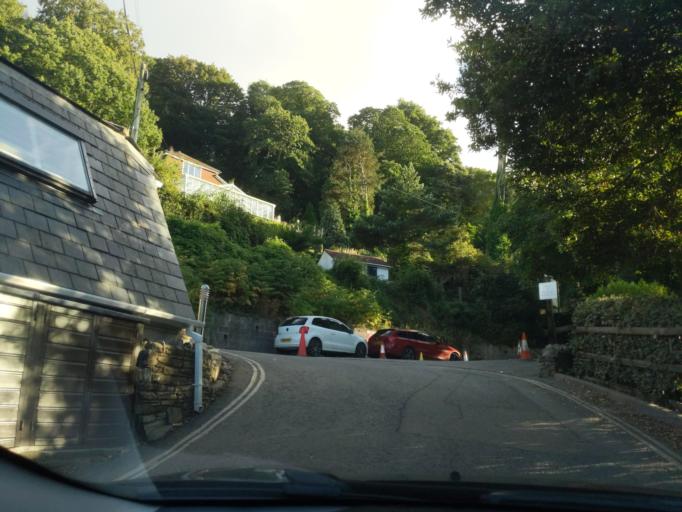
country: GB
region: England
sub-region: Devon
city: Salcombe
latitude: 50.2246
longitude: -3.7846
